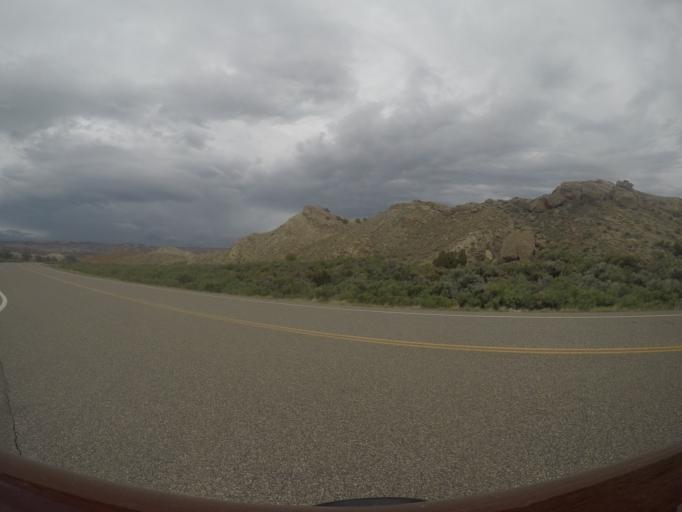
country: US
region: Wyoming
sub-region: Big Horn County
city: Lovell
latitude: 44.9582
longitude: -108.2903
